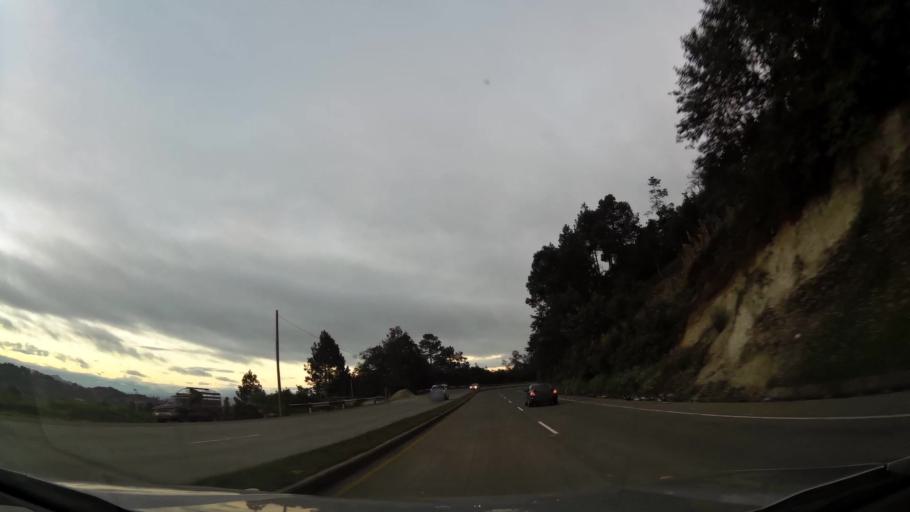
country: GT
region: Solola
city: Concepcion
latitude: 14.8338
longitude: -91.0764
